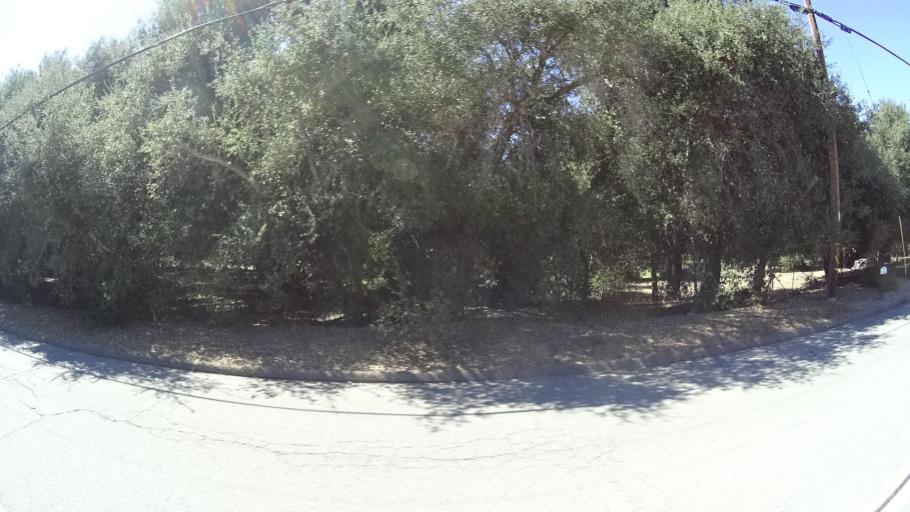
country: US
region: California
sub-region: San Diego County
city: Alpine
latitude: 32.7495
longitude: -116.7585
